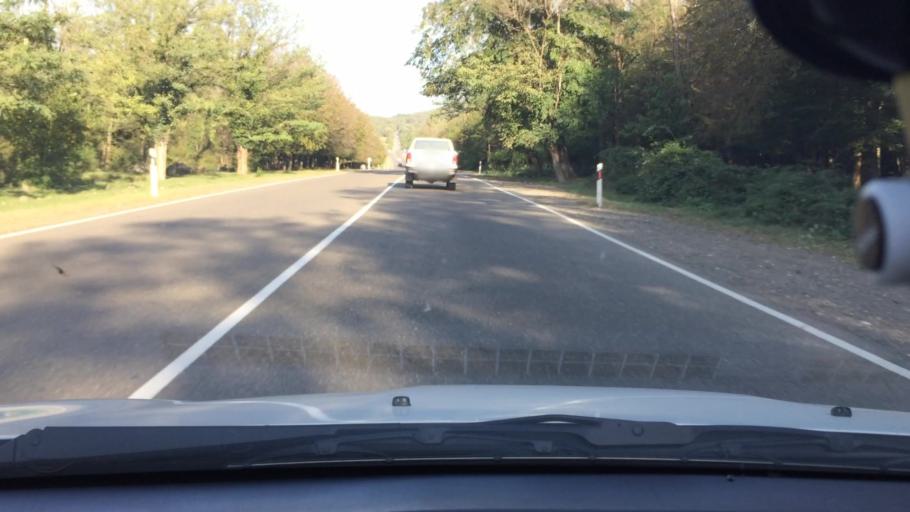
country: GE
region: Imereti
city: Kutaisi
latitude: 42.2343
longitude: 42.7731
